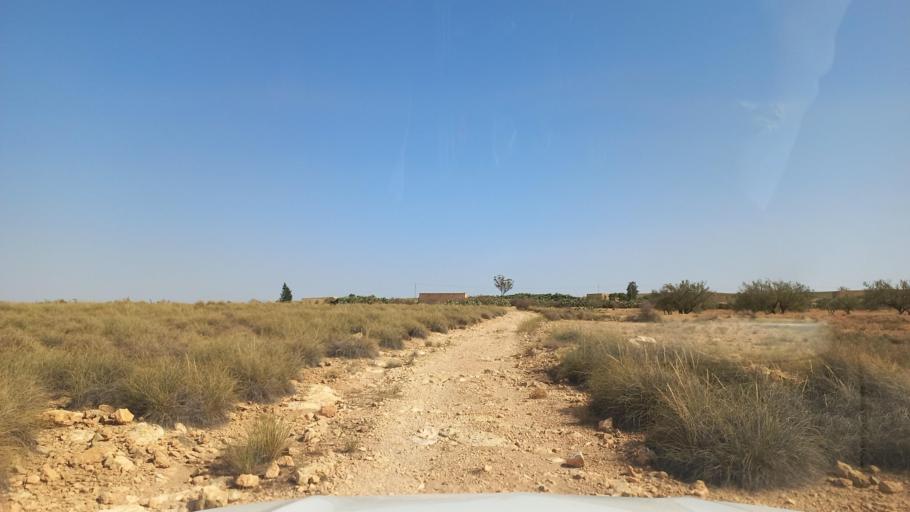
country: TN
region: Al Qasrayn
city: Kasserine
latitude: 35.2135
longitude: 8.9849
